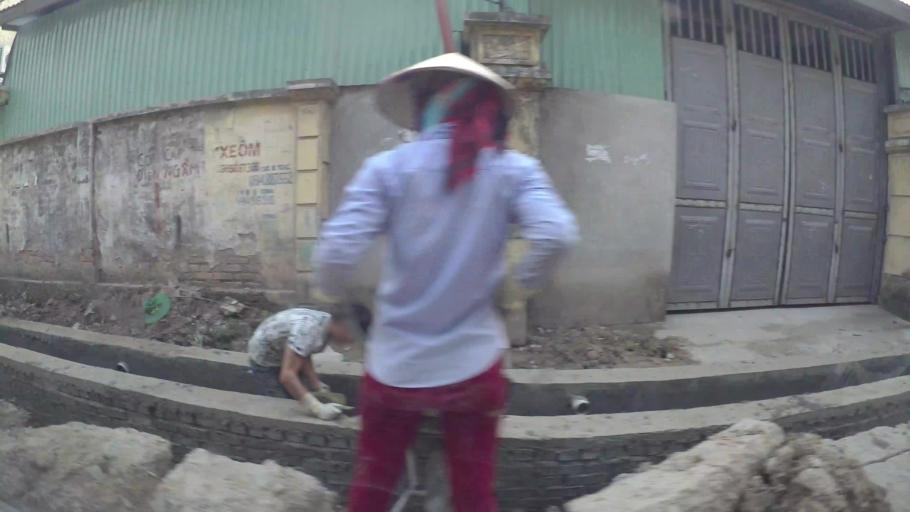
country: VN
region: Ha Noi
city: Cau Dien
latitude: 20.9980
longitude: 105.7296
